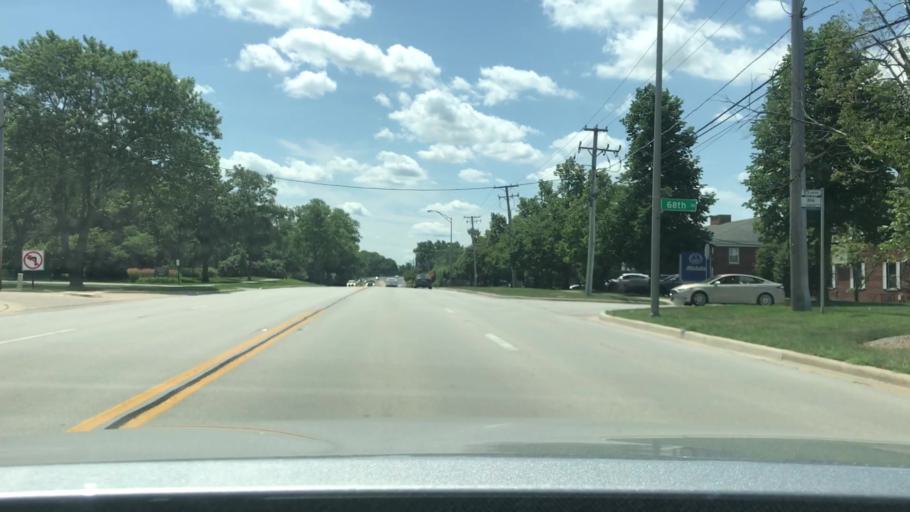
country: US
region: Illinois
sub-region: DuPage County
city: Darien
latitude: 41.7629
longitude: -88.0082
